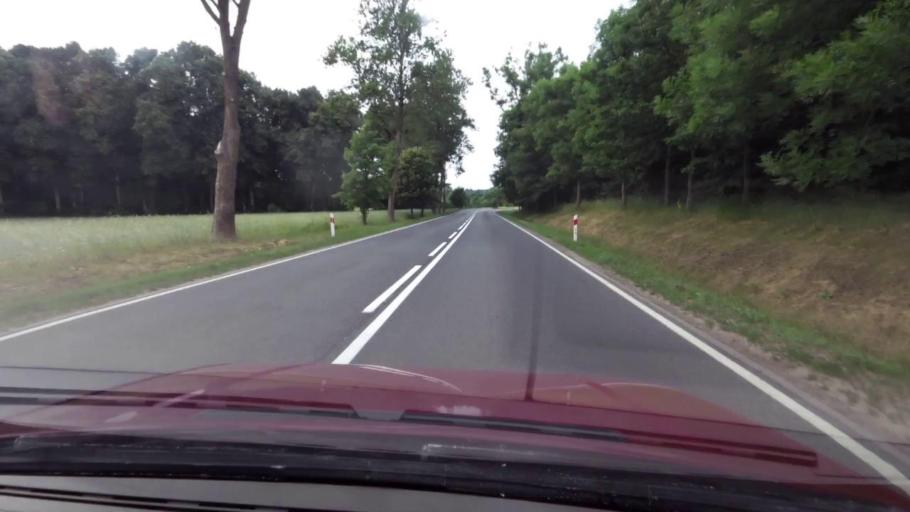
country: PL
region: Pomeranian Voivodeship
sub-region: Powiat bytowski
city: Trzebielino
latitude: 54.2706
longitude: 17.0980
